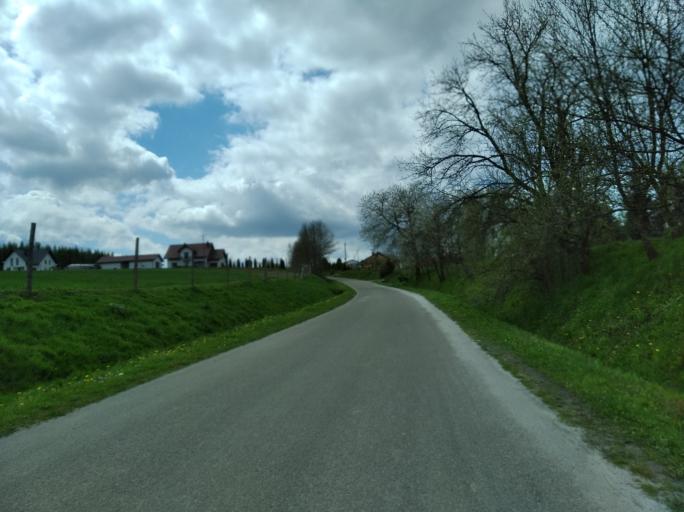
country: PL
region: Subcarpathian Voivodeship
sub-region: Powiat strzyzowski
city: Niebylec
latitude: 49.8806
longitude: 21.9131
